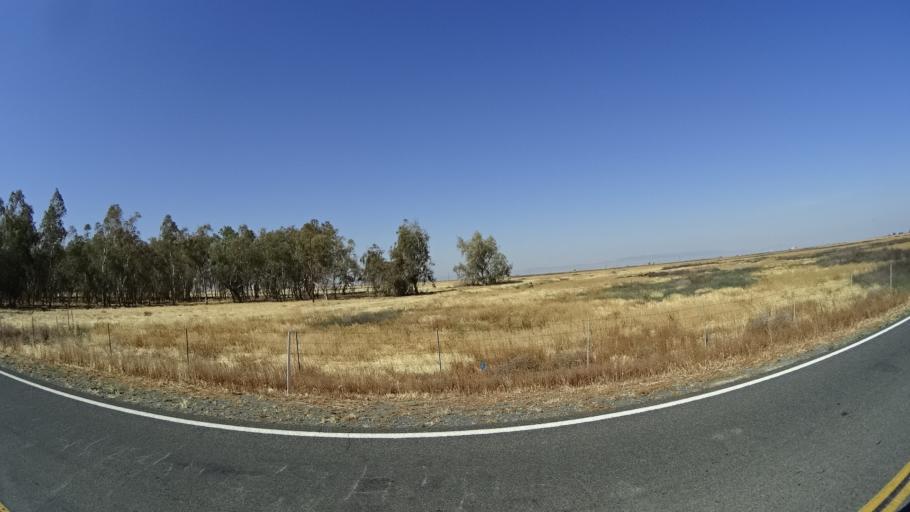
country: US
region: California
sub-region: Fresno County
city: Riverdale
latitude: 36.3635
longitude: -119.9161
